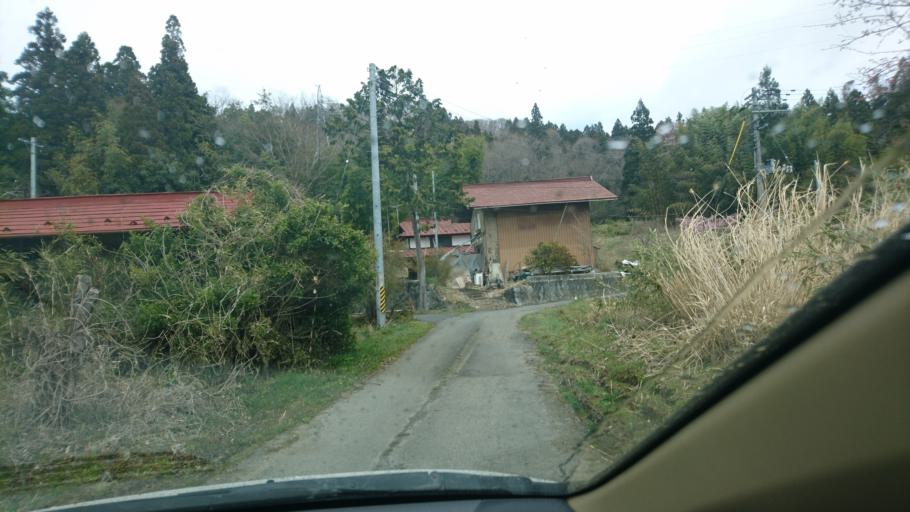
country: JP
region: Iwate
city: Ichinoseki
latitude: 38.9437
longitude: 141.0801
